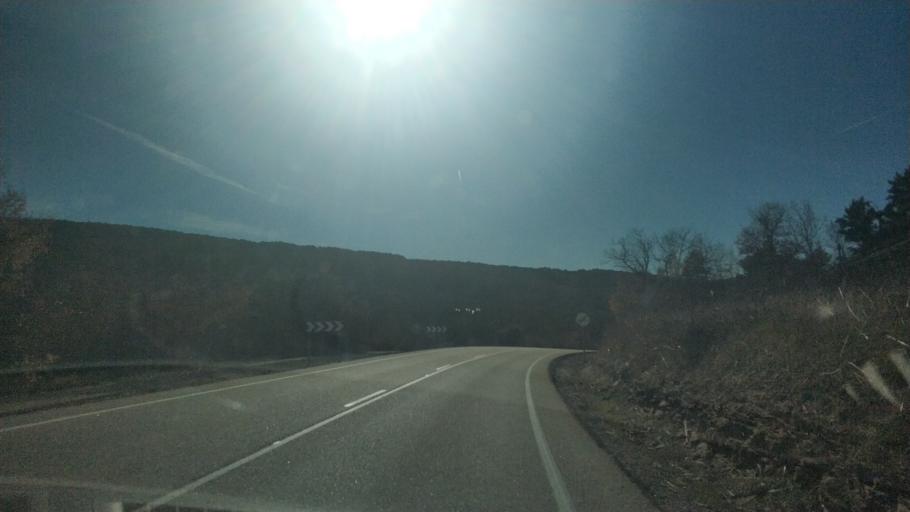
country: ES
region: Castille and Leon
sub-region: Provincia de Soria
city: Vinuesa
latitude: 41.8985
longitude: -2.7703
